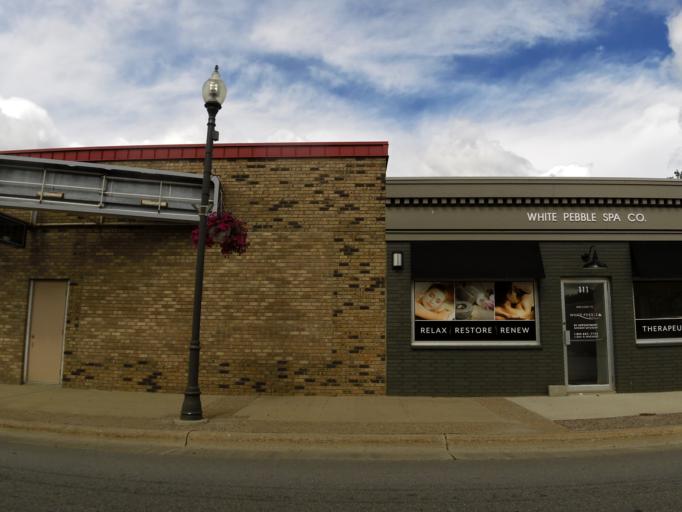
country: US
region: Minnesota
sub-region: Olmsted County
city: Stewartville
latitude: 43.8559
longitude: -92.4885
